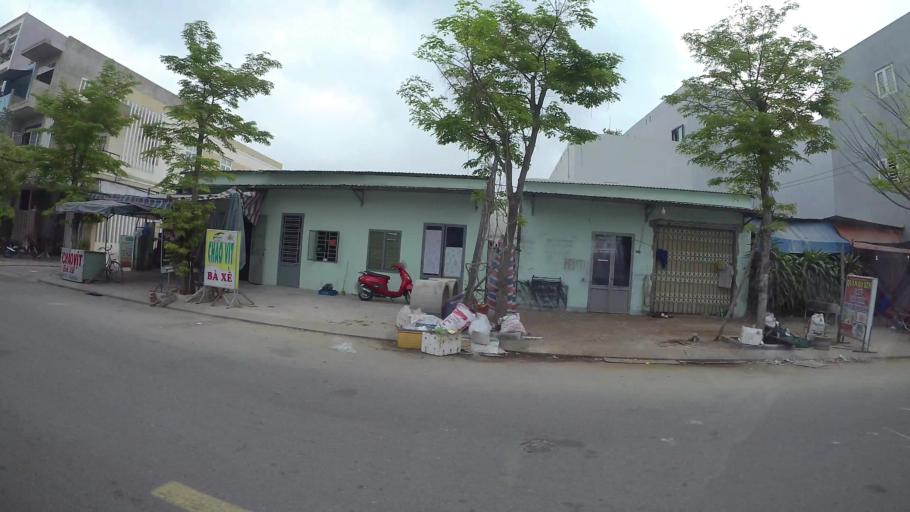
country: VN
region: Da Nang
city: Son Tra
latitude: 16.0848
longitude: 108.2424
